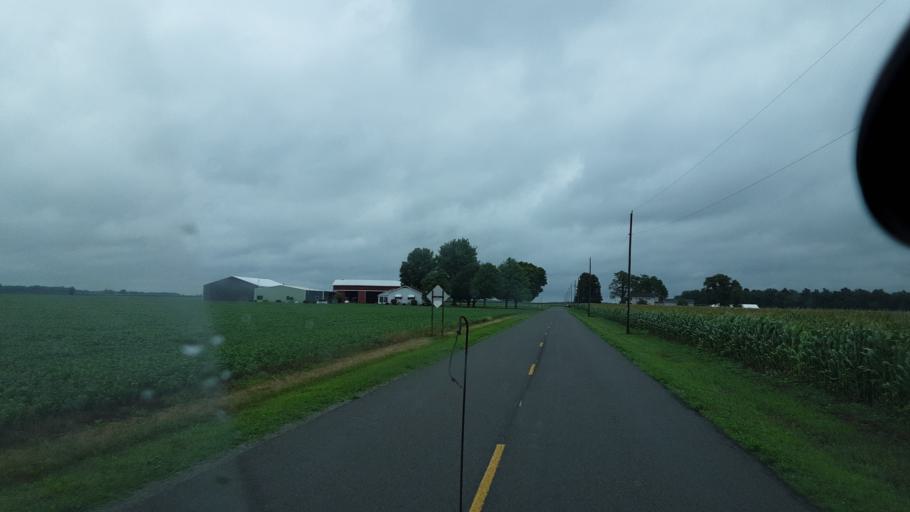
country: US
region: Ohio
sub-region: Van Wert County
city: Convoy
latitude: 40.8018
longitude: -84.6857
